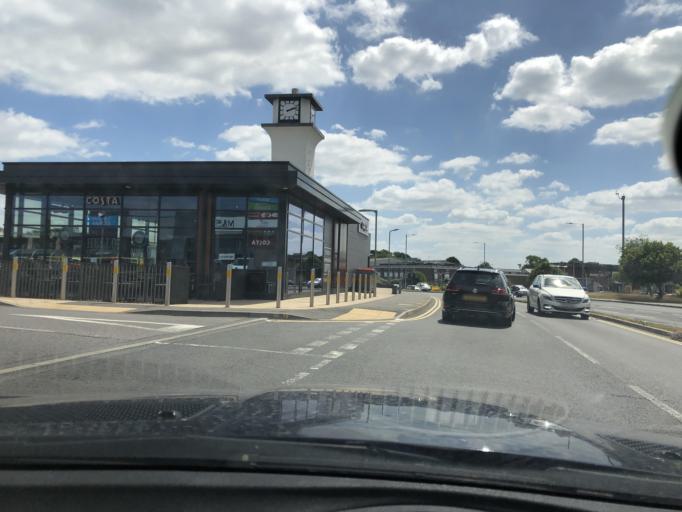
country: GB
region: England
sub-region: Essex
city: Chelmsford
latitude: 51.7234
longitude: 0.4510
